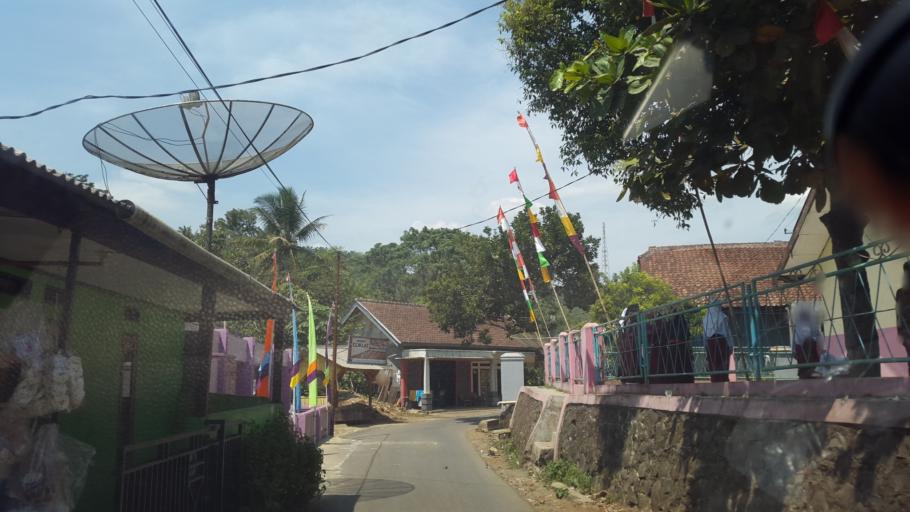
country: ID
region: West Java
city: Sindangsari
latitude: -6.8953
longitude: 106.6509
